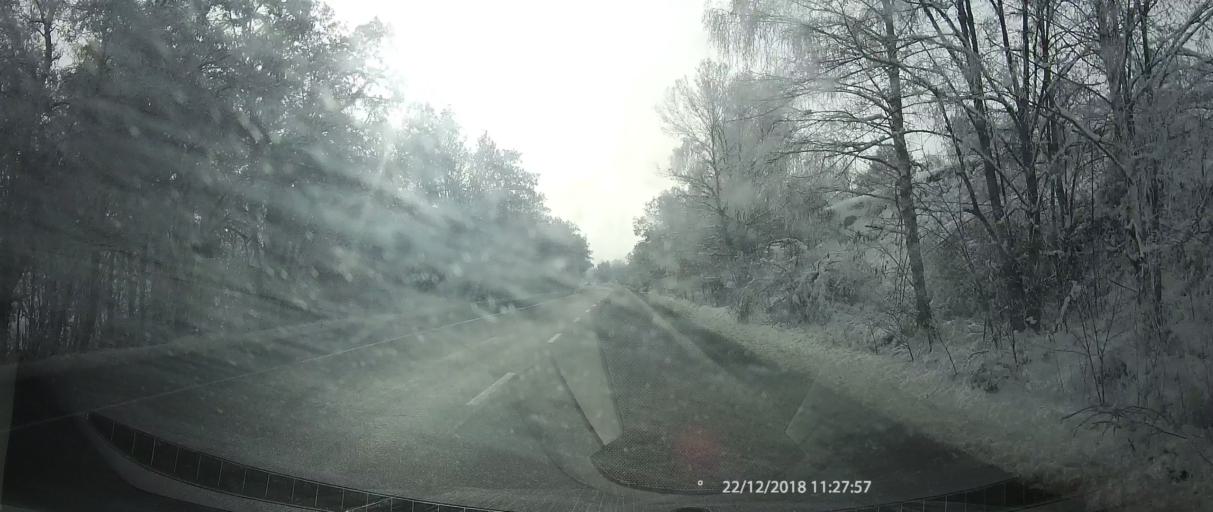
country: BG
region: Kyustendil
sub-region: Obshtina Bobovdol
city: Bobovdol
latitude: 42.2733
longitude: 22.9427
